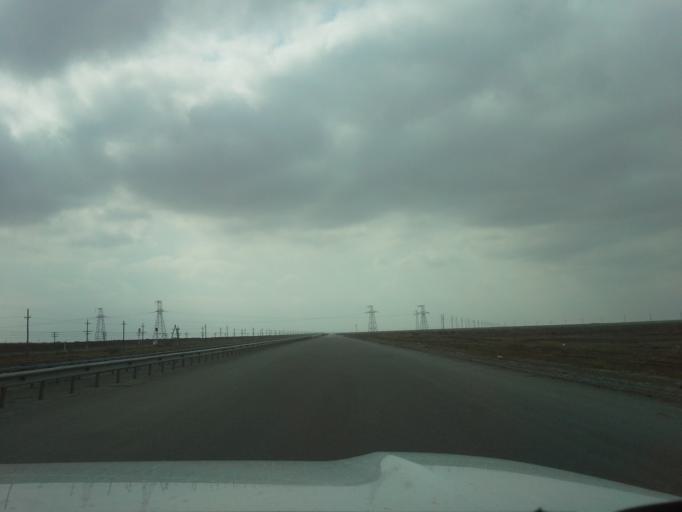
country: IR
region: Razavi Khorasan
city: Kalat-e Naderi
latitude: 37.2163
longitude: 60.0974
